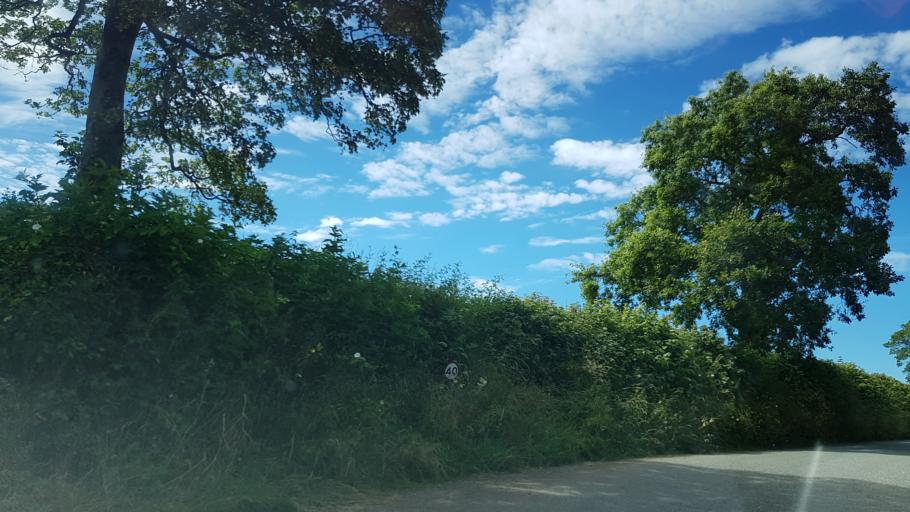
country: GB
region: Wales
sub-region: Pembrokeshire
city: Haverfordwest
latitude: 51.8207
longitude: -4.9437
